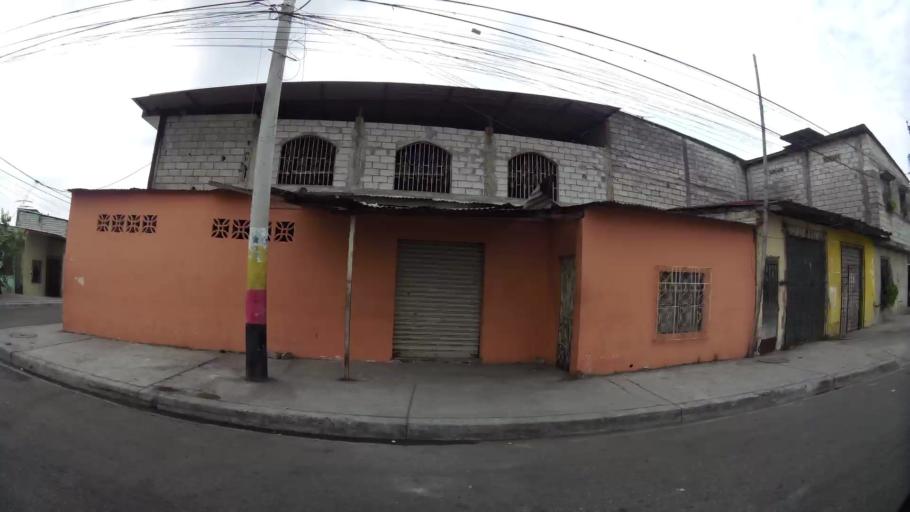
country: EC
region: Guayas
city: Guayaquil
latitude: -2.2315
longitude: -79.9103
